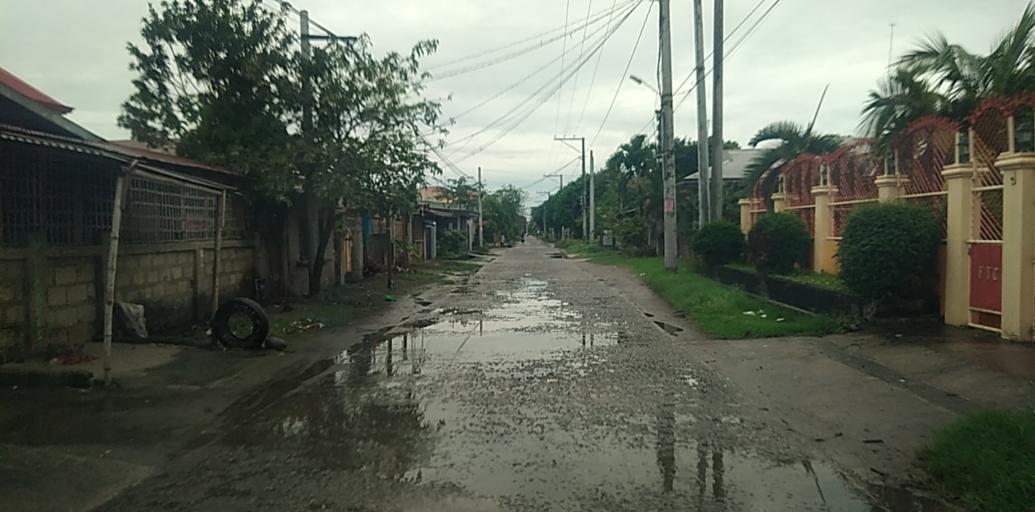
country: PH
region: Central Luzon
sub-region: Province of Pampanga
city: Arayat
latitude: 15.1503
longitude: 120.7418
